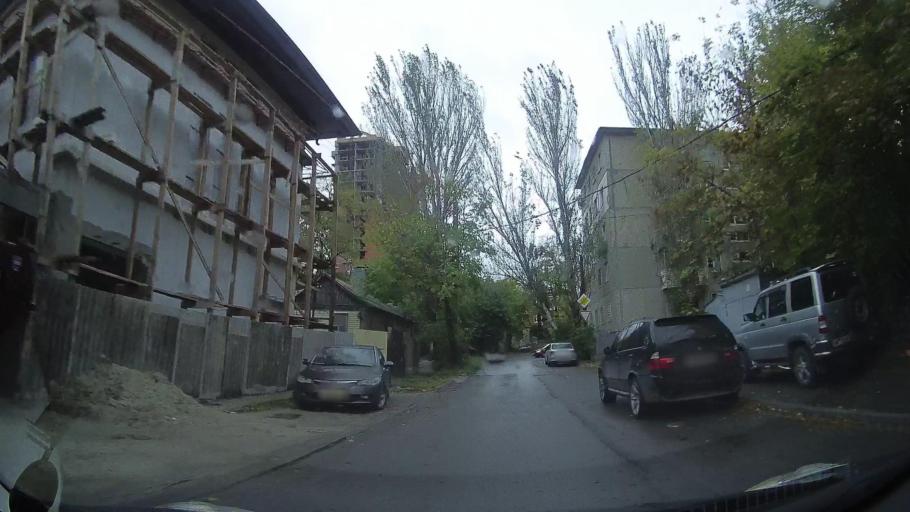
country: RU
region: Rostov
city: Rostov-na-Donu
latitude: 47.2336
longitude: 39.6935
